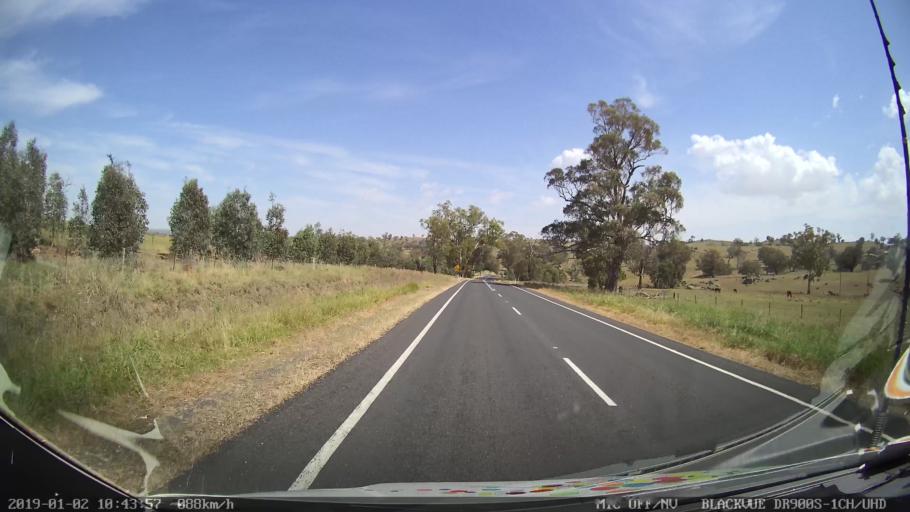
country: AU
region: New South Wales
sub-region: Cootamundra
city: Cootamundra
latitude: -34.7663
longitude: 148.3002
